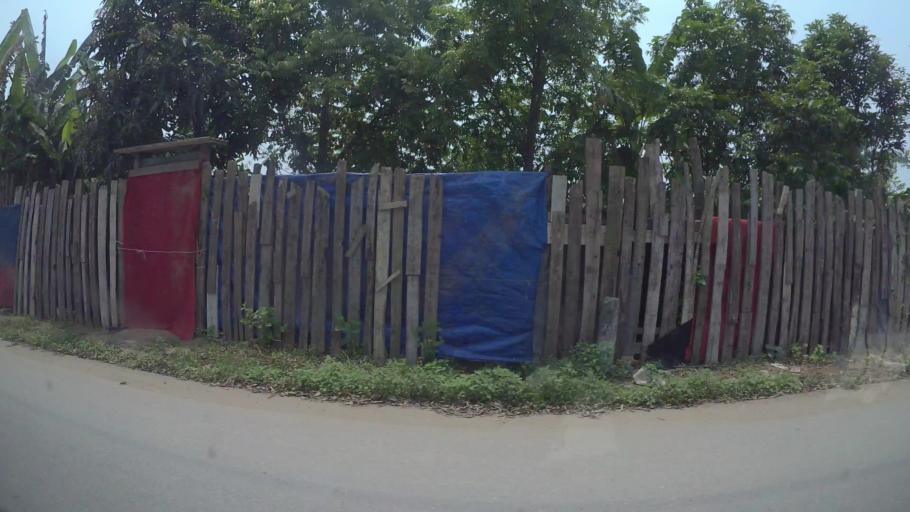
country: VN
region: Ha Noi
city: Ha Dong
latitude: 20.9972
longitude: 105.7685
